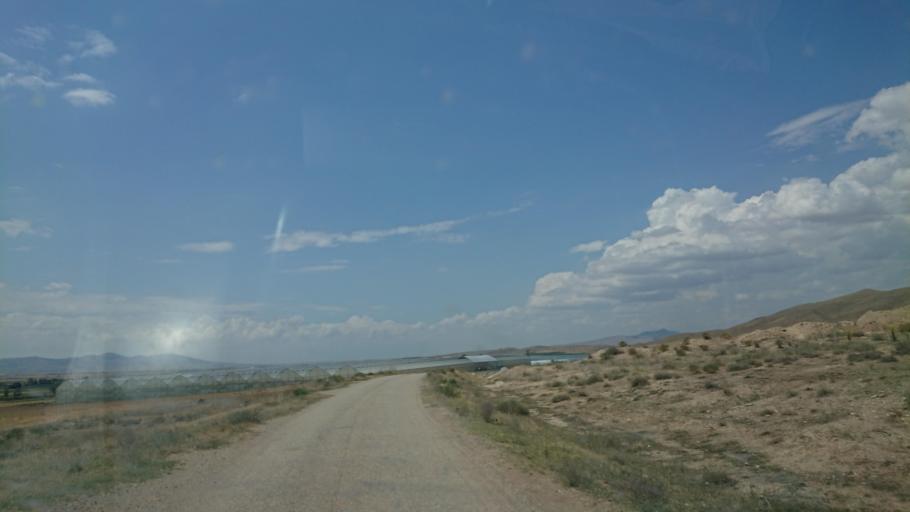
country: TR
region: Aksaray
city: Sariyahsi
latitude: 38.9968
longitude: 33.9146
